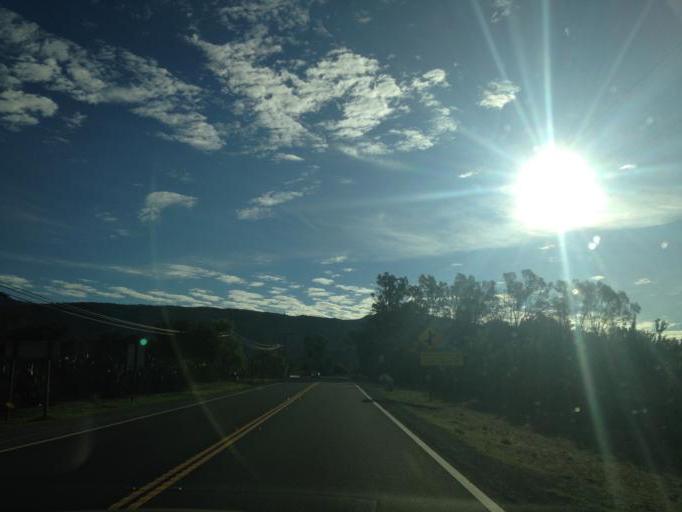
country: US
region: California
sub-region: San Diego County
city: Valley Center
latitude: 33.2888
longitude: -116.9611
